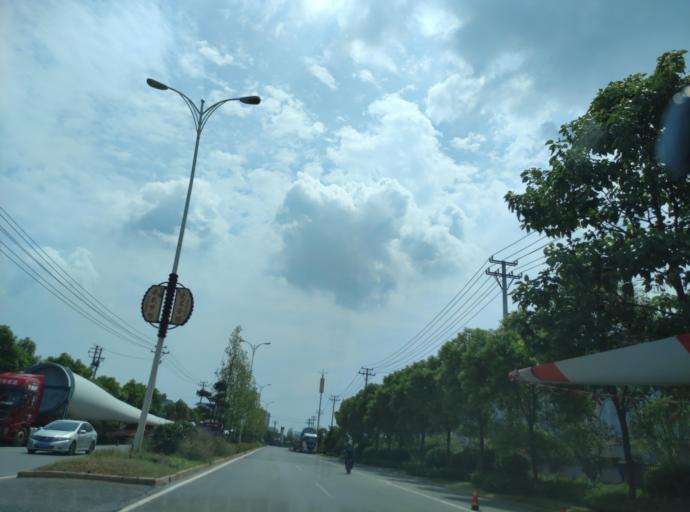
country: CN
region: Jiangxi Sheng
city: Yuannan
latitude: 27.6649
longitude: 114.0118
